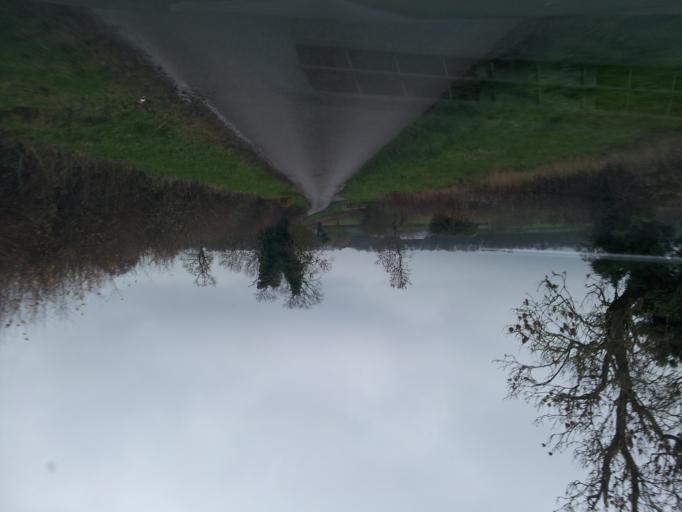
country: GB
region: England
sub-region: Warwickshire
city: Rugby
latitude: 52.3417
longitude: -1.1931
